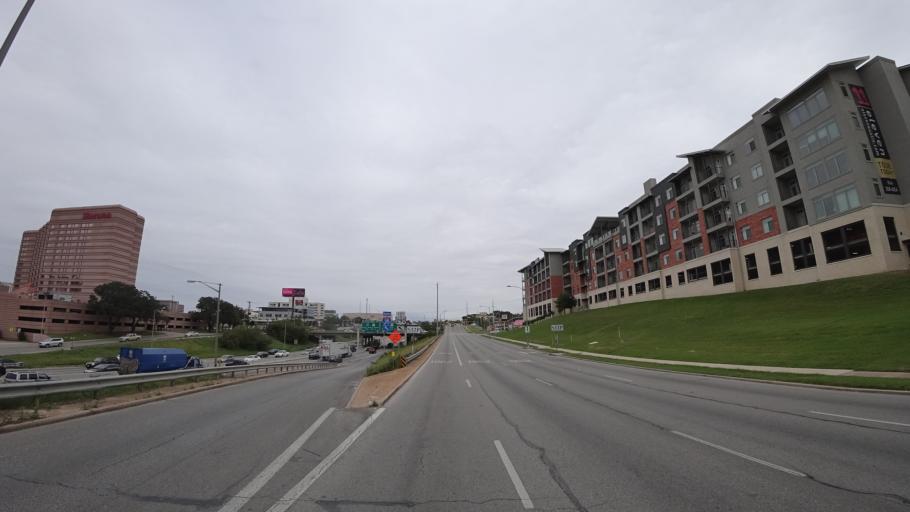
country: US
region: Texas
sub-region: Travis County
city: Austin
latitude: 30.2689
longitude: -97.7331
